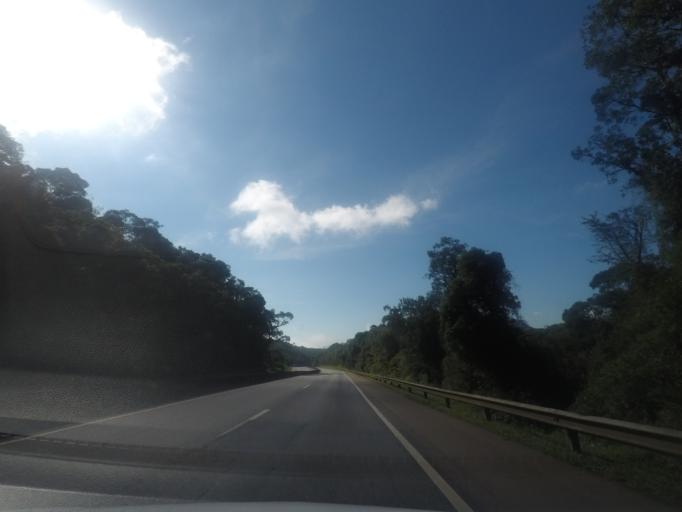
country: BR
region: Parana
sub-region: Piraquara
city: Piraquara
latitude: -25.5918
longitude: -48.9270
